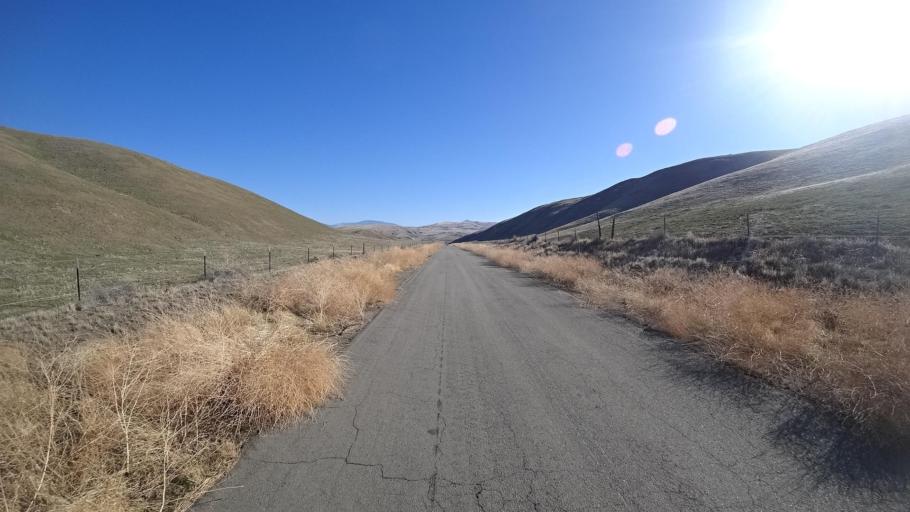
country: US
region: California
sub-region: Kern County
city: Maricopa
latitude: 34.9806
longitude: -119.4676
